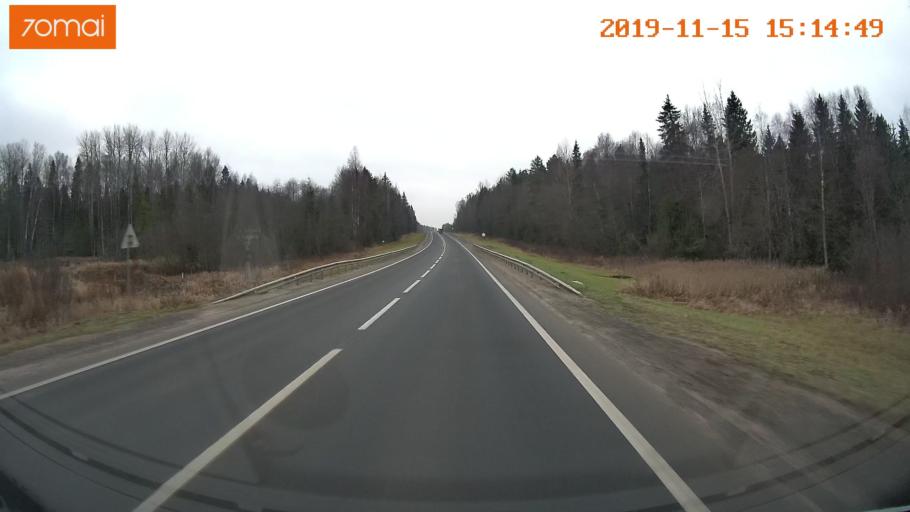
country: RU
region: Jaroslavl
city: Danilov
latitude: 58.2942
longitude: 40.2018
